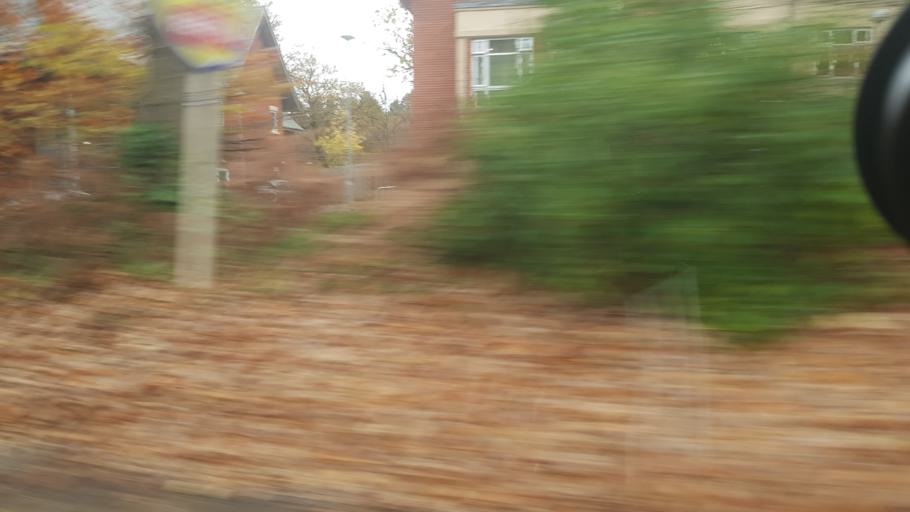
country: GB
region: England
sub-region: Hampshire
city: Farnborough
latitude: 51.3162
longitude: -0.7773
